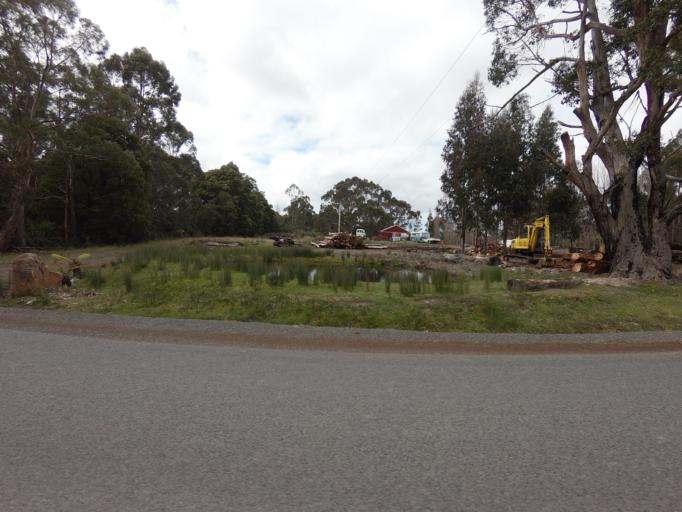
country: AU
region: Tasmania
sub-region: Huon Valley
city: Geeveston
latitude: -43.4306
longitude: 146.9035
